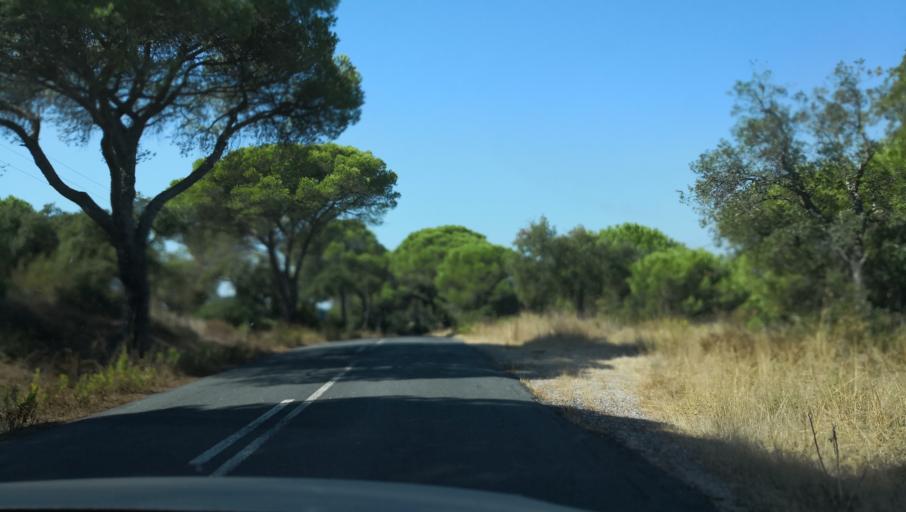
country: PT
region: Setubal
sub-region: Alcacer do Sal
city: Alcacer do Sal
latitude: 38.3038
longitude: -8.4148
